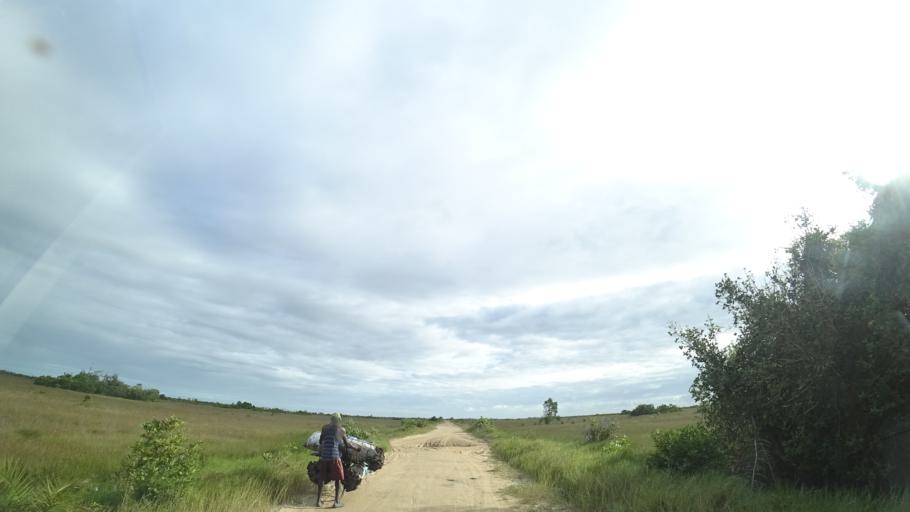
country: MZ
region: Sofala
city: Beira
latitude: -19.6956
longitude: 35.0341
